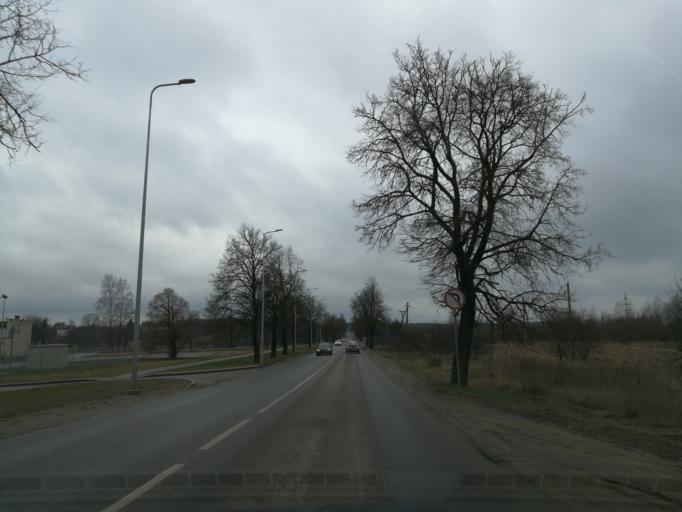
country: LT
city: Grigiskes
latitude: 54.6462
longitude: 25.1372
